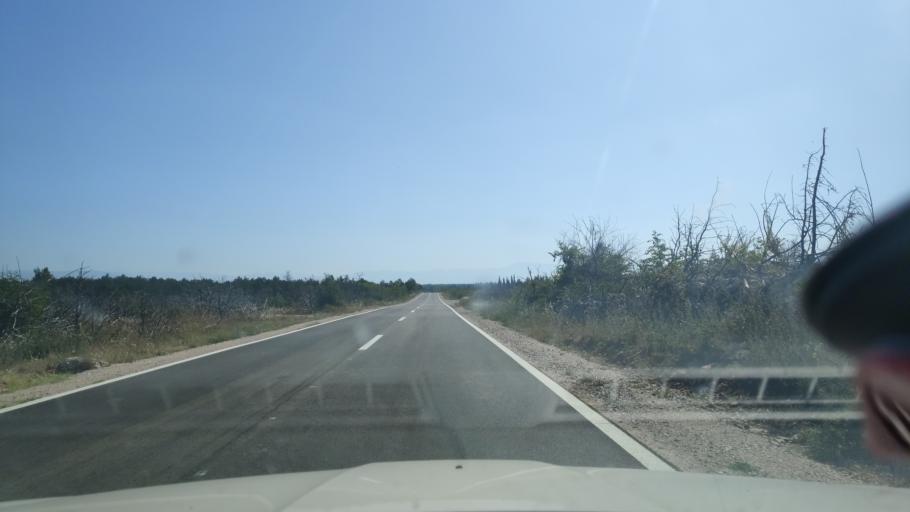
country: HR
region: Sibensko-Kniniska
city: Kistanje
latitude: 43.9456
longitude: 15.8353
